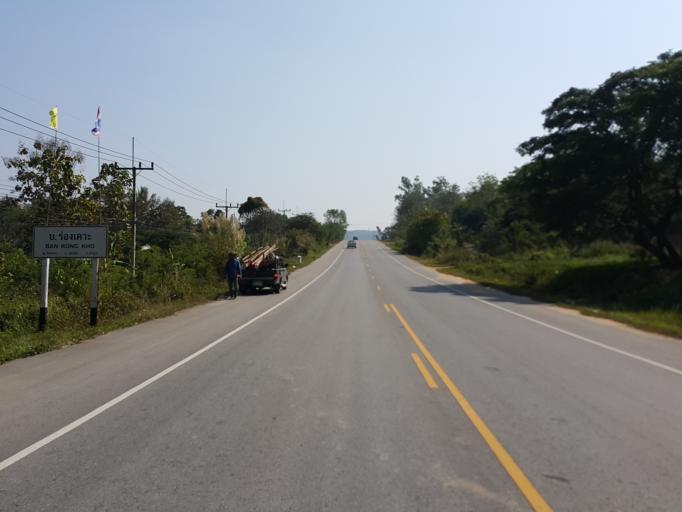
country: TH
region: Lampang
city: Wang Nuea
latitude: 18.9963
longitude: 99.6137
